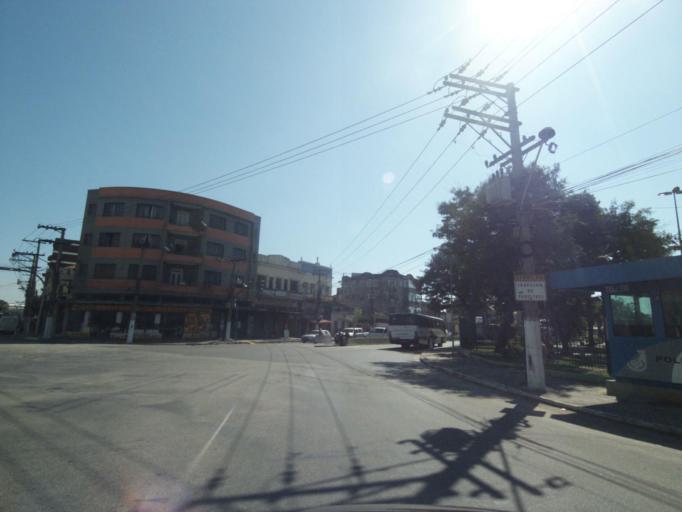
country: BR
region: Rio de Janeiro
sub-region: Niteroi
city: Niteroi
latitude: -22.8600
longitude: -43.1015
